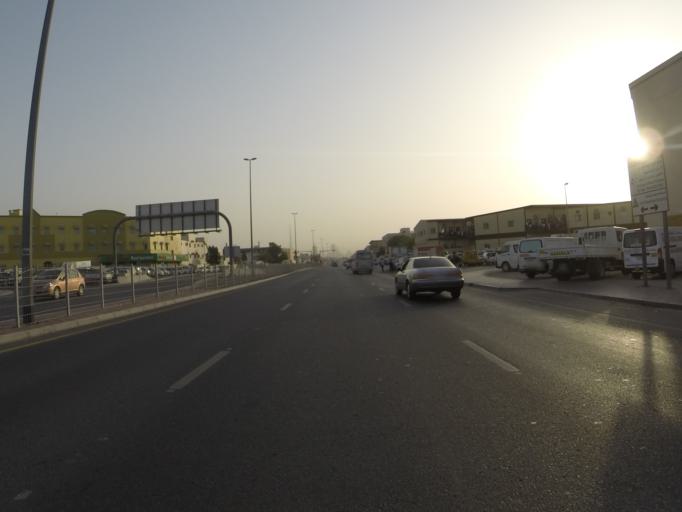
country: AE
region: Dubai
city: Dubai
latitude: 25.1309
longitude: 55.2333
